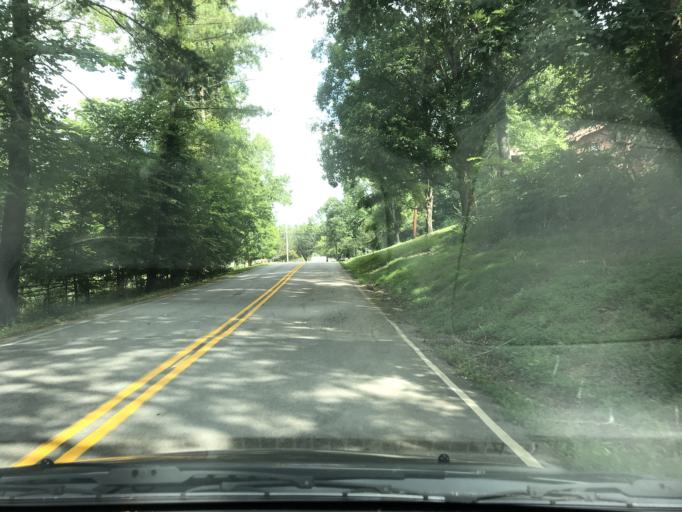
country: US
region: Tennessee
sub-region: Hamilton County
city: Lakesite
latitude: 35.1865
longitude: -85.1037
